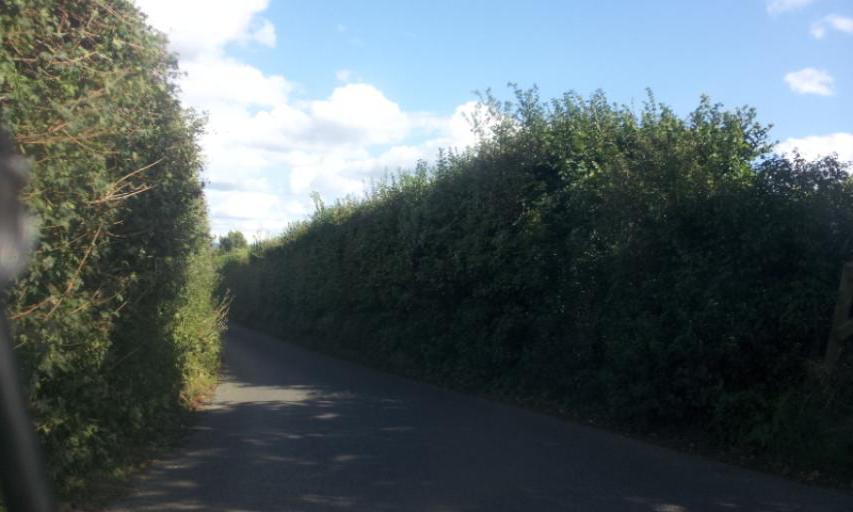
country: GB
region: England
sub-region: Kent
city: Snodland
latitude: 51.3238
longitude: 0.4241
